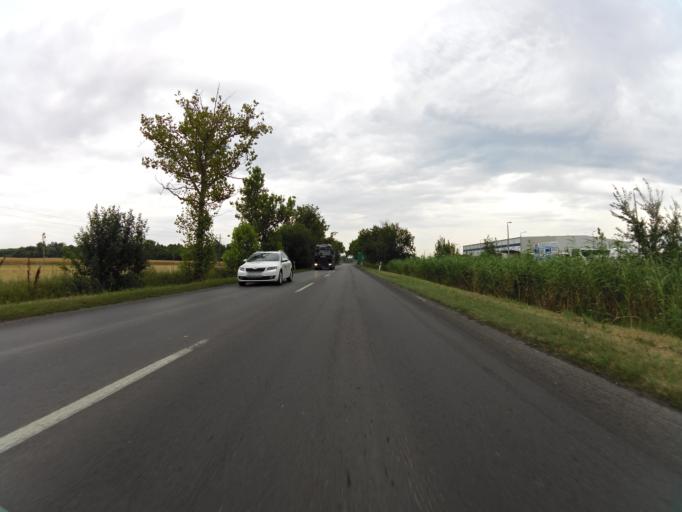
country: HU
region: Csongrad
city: Szeged
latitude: 46.2859
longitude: 20.0892
